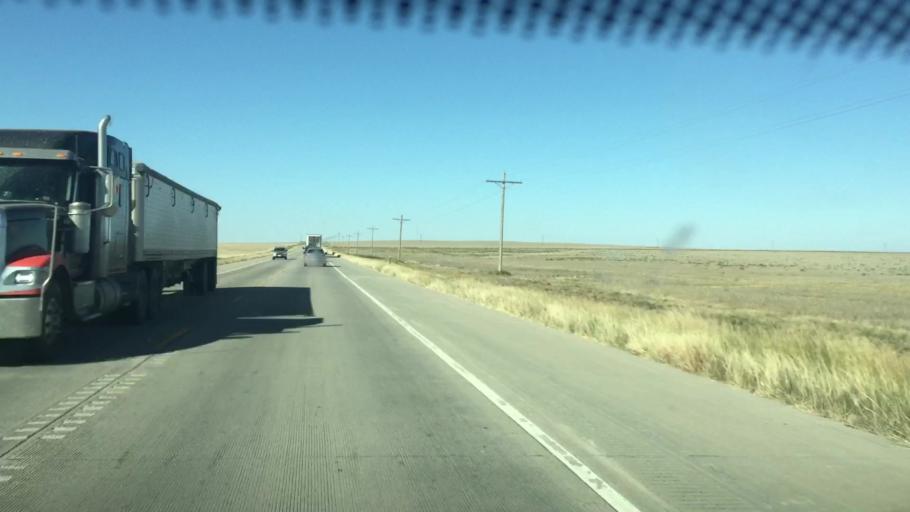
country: US
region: Colorado
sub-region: Prowers County
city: Lamar
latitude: 38.2468
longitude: -102.7240
